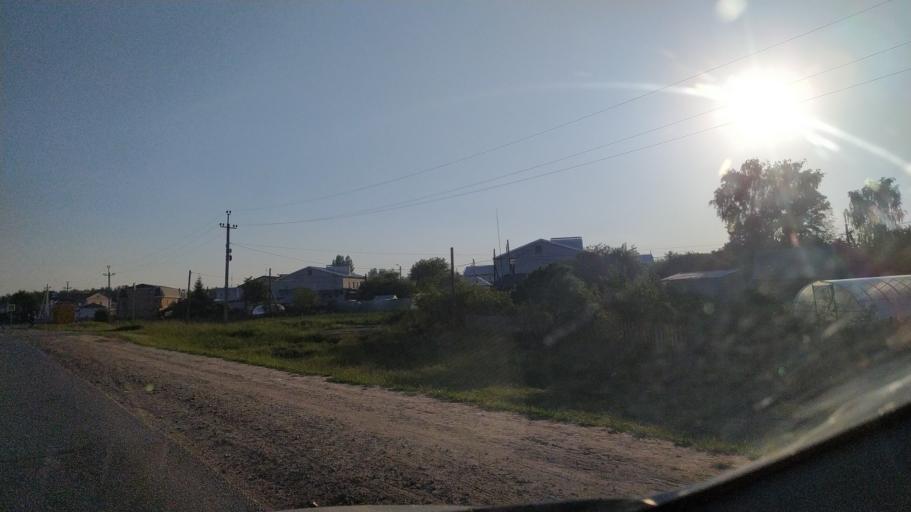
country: RU
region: Chuvashia
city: Kugesi
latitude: 56.0389
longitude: 47.3200
